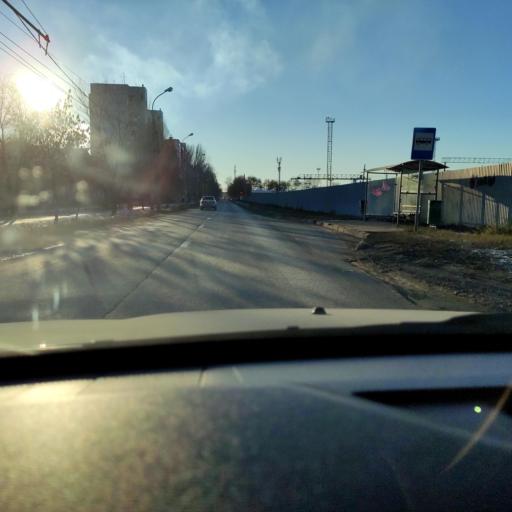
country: RU
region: Samara
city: Samara
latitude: 53.1194
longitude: 50.0741
